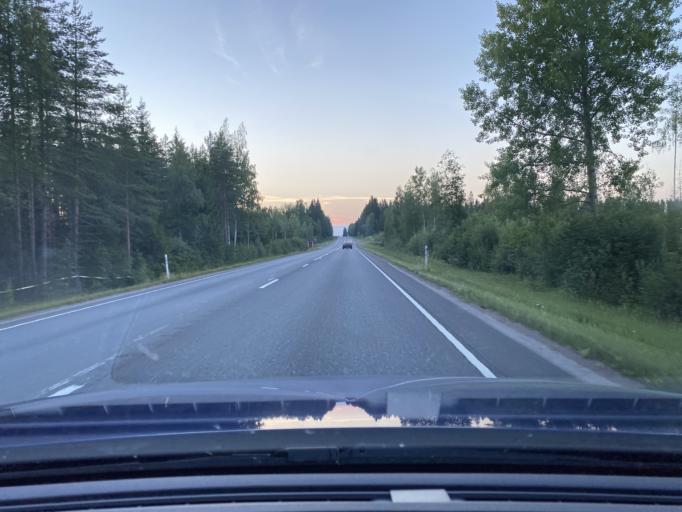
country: FI
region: Pirkanmaa
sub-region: Luoteis-Pirkanmaa
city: Ikaalinen
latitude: 61.8331
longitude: 22.9409
